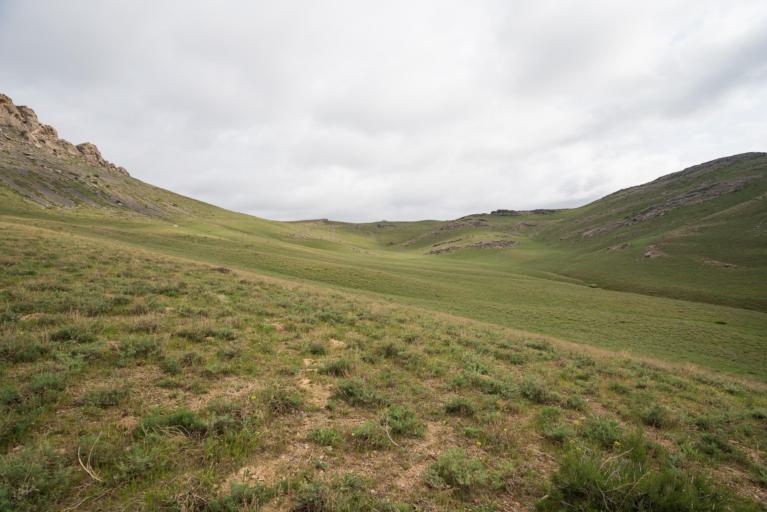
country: KZ
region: Ongtustik Qazaqstan
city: Ashchysay
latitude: 43.5964
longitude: 68.9187
